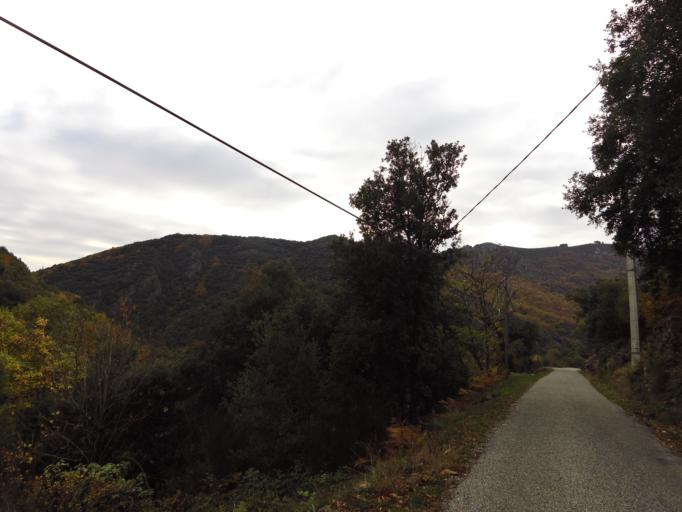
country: FR
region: Rhone-Alpes
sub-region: Departement de l'Ardeche
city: Les Vans
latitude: 44.4944
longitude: 4.0495
